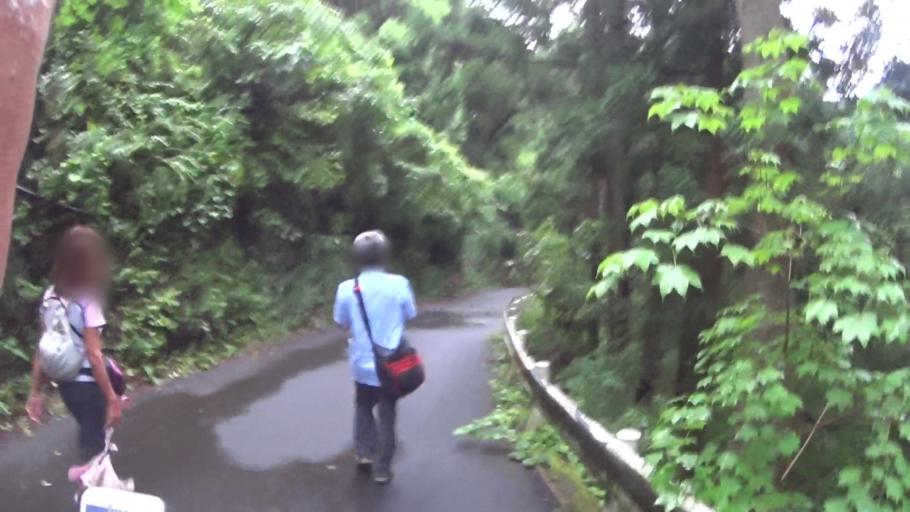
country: JP
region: Tokyo
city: Itsukaichi
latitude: 35.8021
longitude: 139.0798
